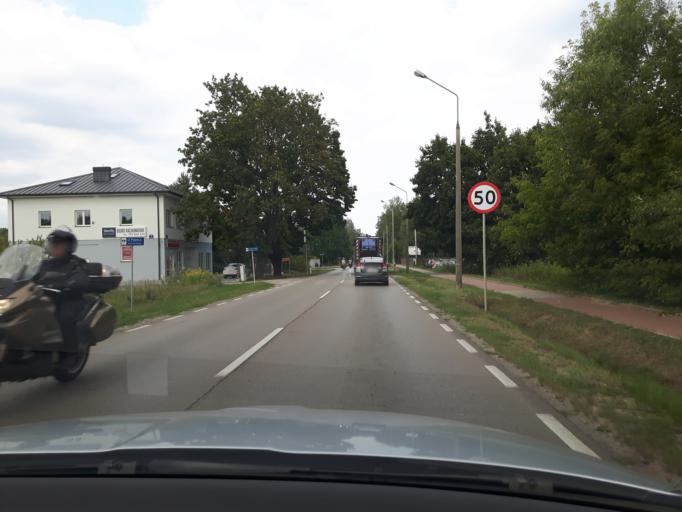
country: PL
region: Masovian Voivodeship
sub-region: Powiat legionowski
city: Stanislawow Pierwszy
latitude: 52.3877
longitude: 21.0311
